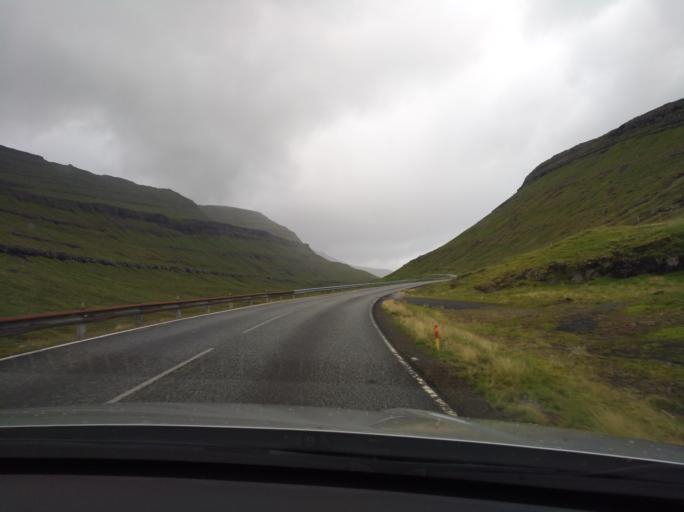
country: FO
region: Eysturoy
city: Fuglafjordur
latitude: 62.2243
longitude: -6.8800
